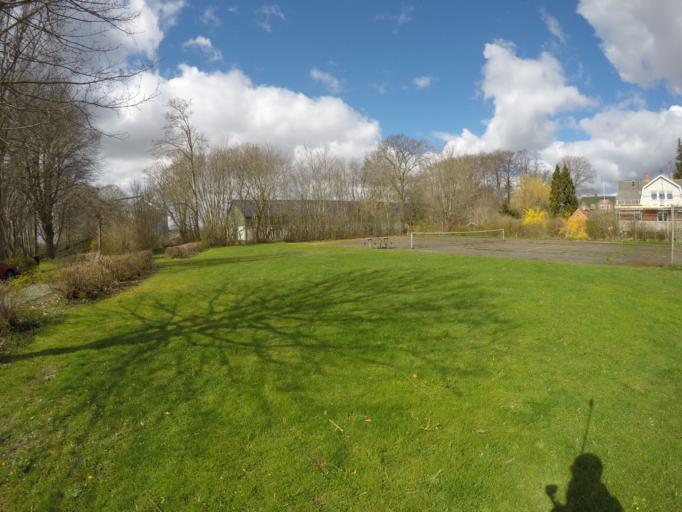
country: SE
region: Skane
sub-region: Ystads Kommun
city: Kopingebro
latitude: 55.4409
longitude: 14.1110
